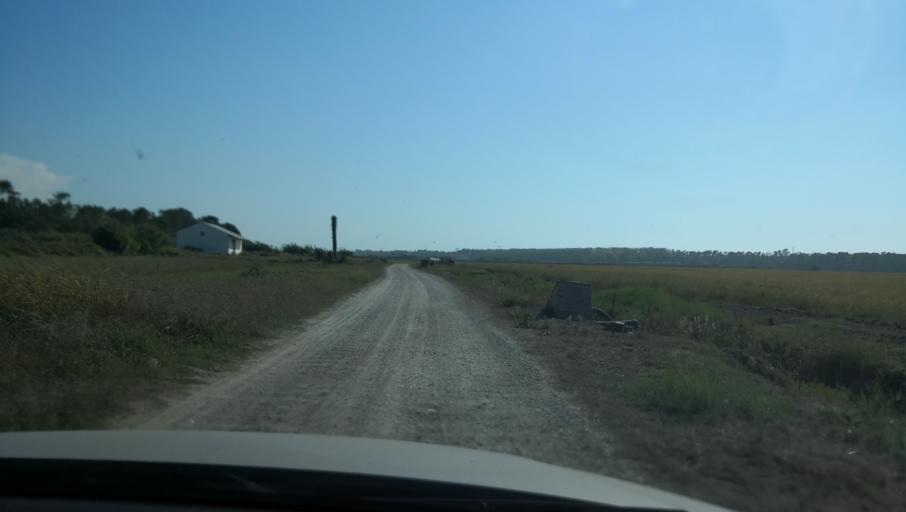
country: PT
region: Setubal
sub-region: Setubal
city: Setubal
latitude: 38.3912
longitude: -8.7895
